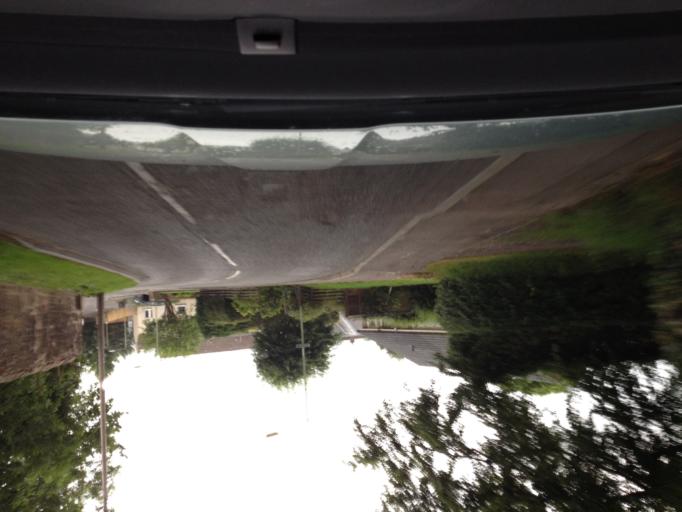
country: GB
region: Scotland
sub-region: Perth and Kinross
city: Bridge of Earn
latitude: 56.3418
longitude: -3.4099
